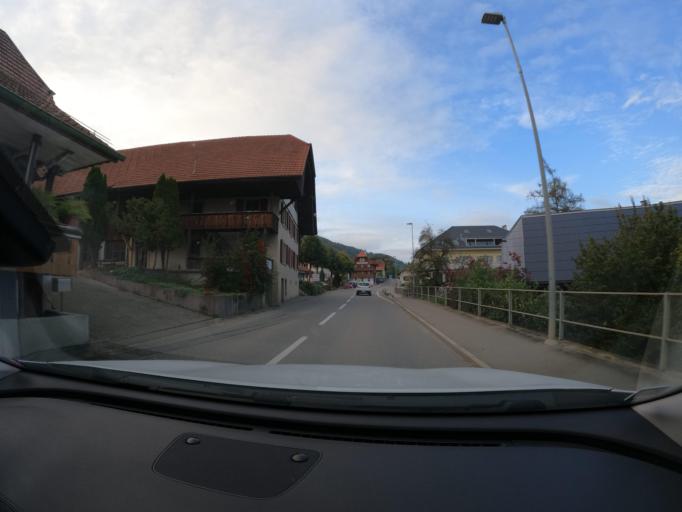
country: CH
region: Bern
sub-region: Bern-Mittelland District
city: Toffen
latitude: 46.8605
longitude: 7.4907
